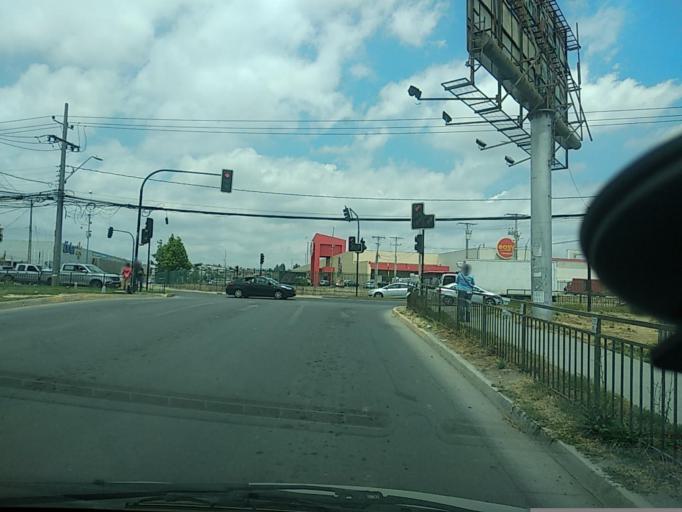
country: CL
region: Valparaiso
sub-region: Provincia de Marga Marga
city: Quilpue
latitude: -33.0439
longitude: -71.4193
